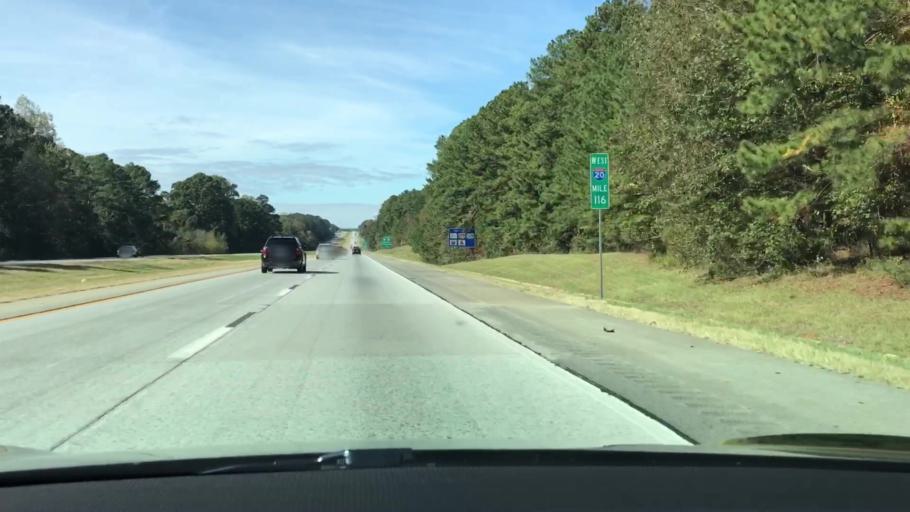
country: US
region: Georgia
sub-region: Morgan County
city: Madison
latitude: 33.5555
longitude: -83.4473
